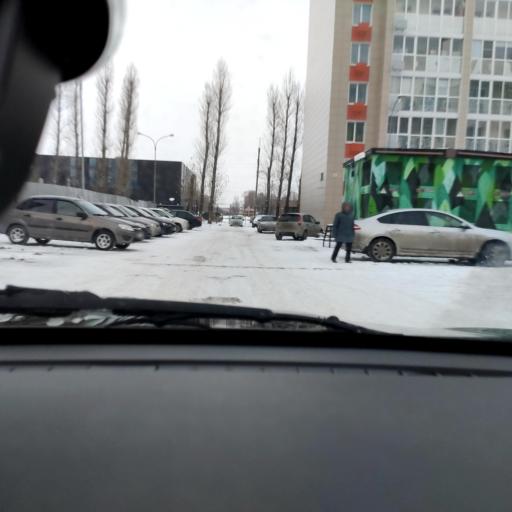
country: RU
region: Samara
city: Tol'yatti
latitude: 53.5484
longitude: 49.3126
